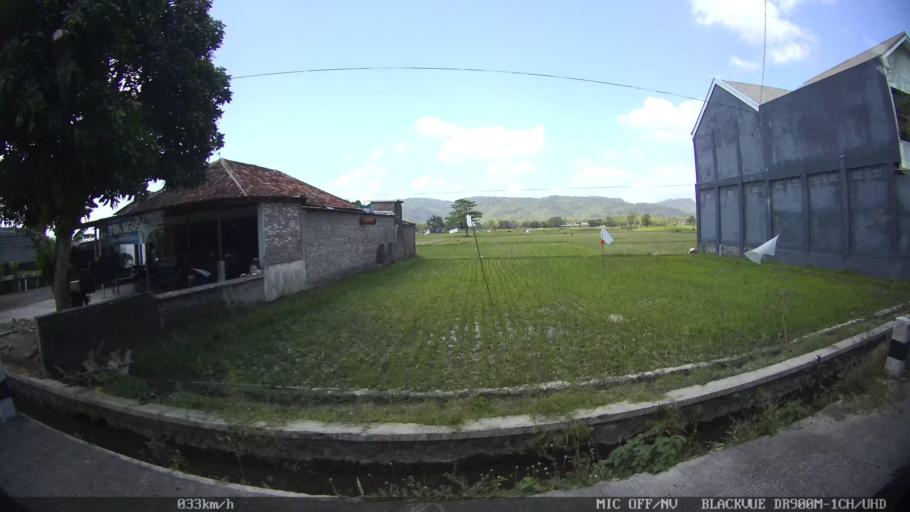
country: ID
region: Daerah Istimewa Yogyakarta
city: Pundong
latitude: -7.9311
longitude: 110.3737
